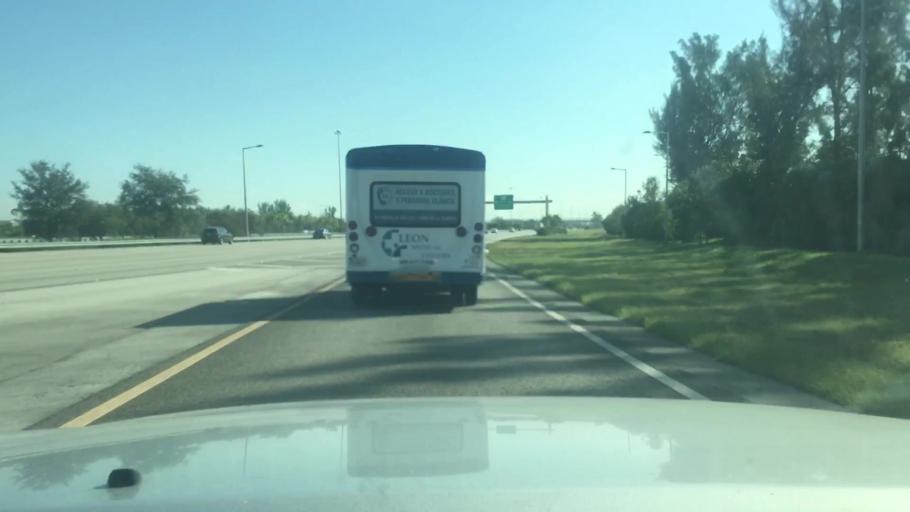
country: US
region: Florida
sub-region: Miami-Dade County
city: Sweetwater
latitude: 25.7805
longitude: -80.3655
